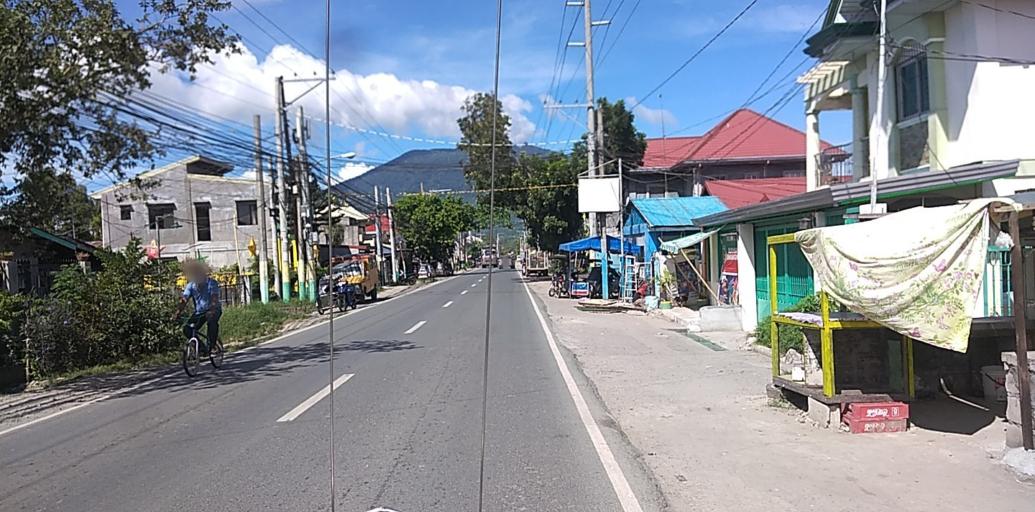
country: PH
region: Central Luzon
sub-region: Province of Pampanga
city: Arayat
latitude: 15.1415
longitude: 120.7722
